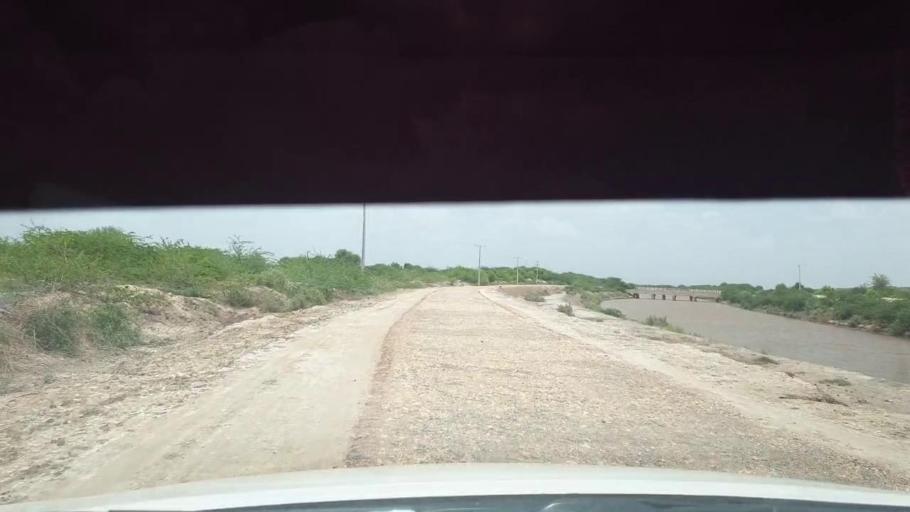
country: PK
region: Sindh
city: Kadhan
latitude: 24.5288
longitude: 69.1255
